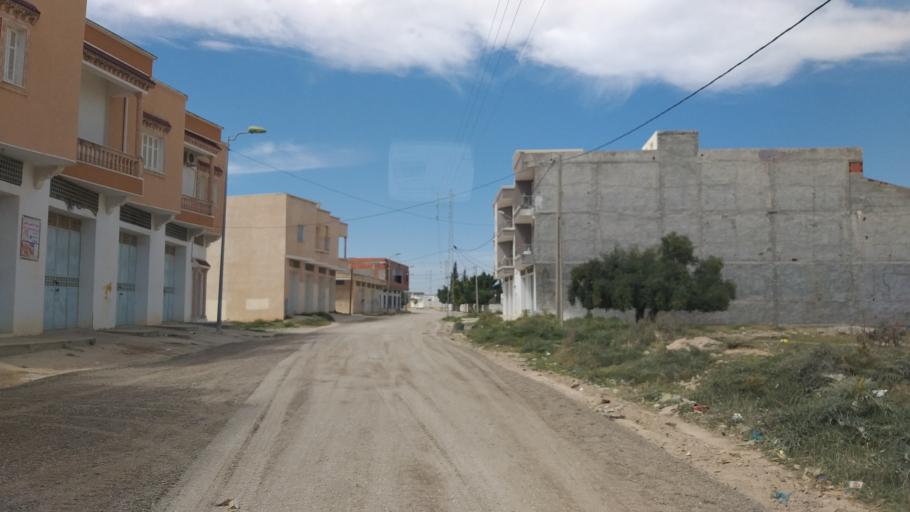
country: TN
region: Al Mahdiyah
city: El Jem
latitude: 35.3037
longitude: 10.6953
